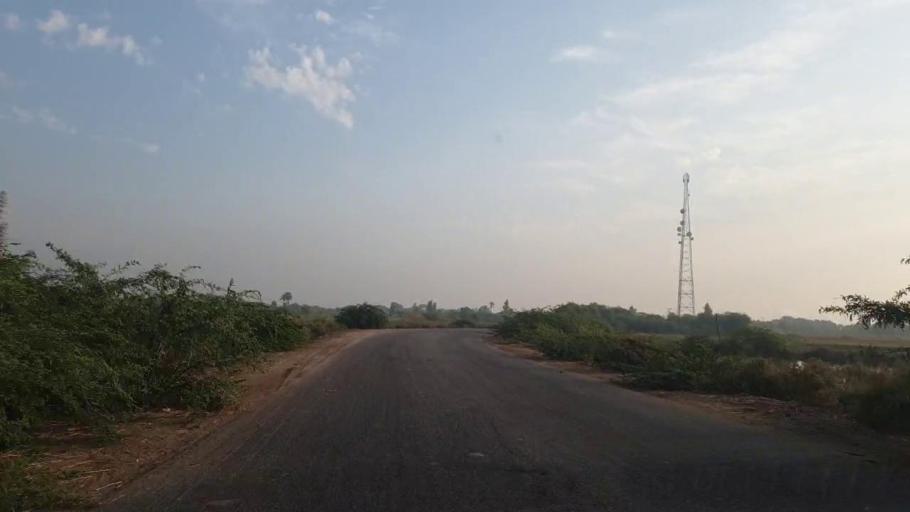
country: PK
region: Sindh
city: Tando Bago
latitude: 24.7065
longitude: 68.9295
